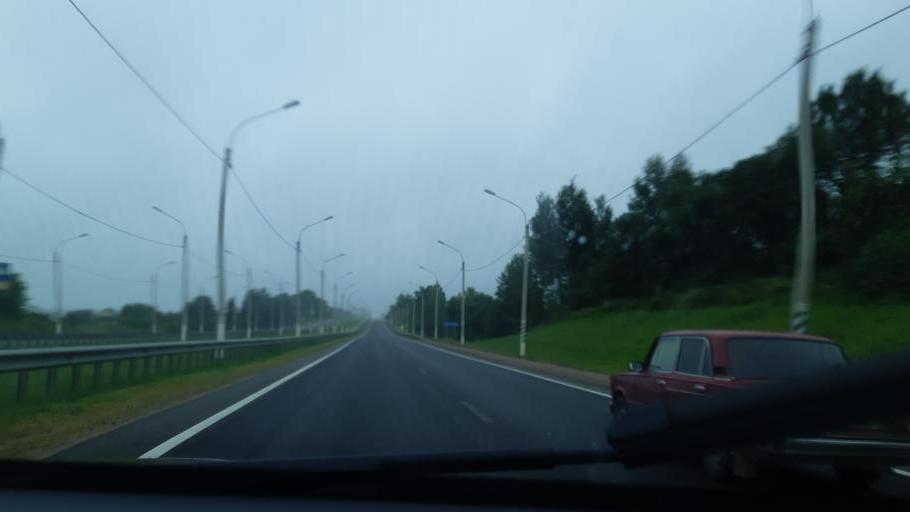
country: RU
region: Smolensk
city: Talashkino
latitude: 54.5869
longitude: 32.2253
